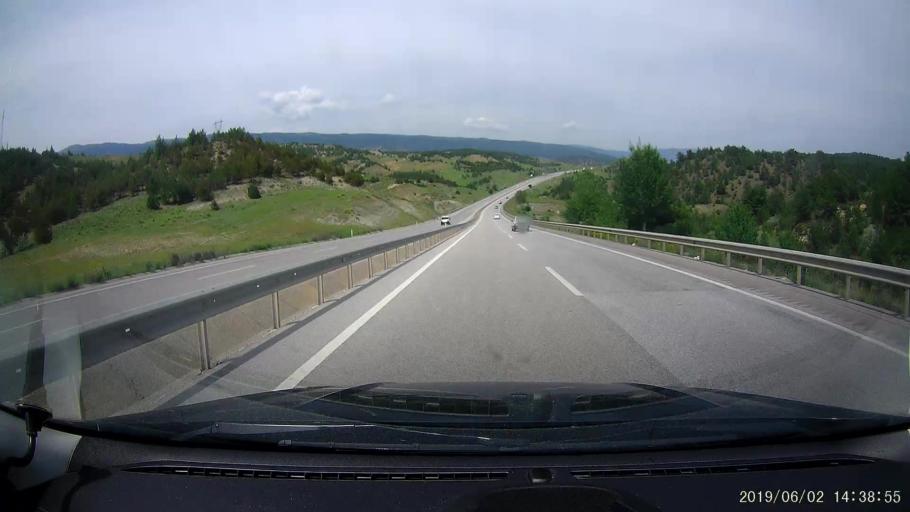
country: TR
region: Corum
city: Hacihamza
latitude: 41.0623
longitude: 34.2900
